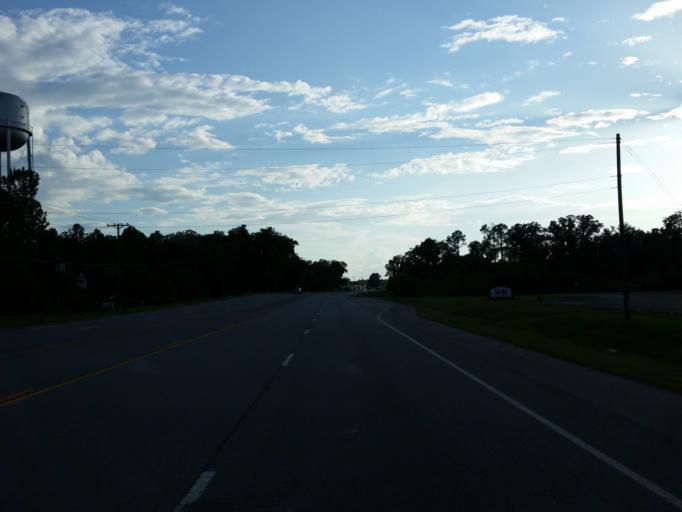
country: US
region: Georgia
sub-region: Clinch County
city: Homerville
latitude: 31.0321
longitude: -82.7665
